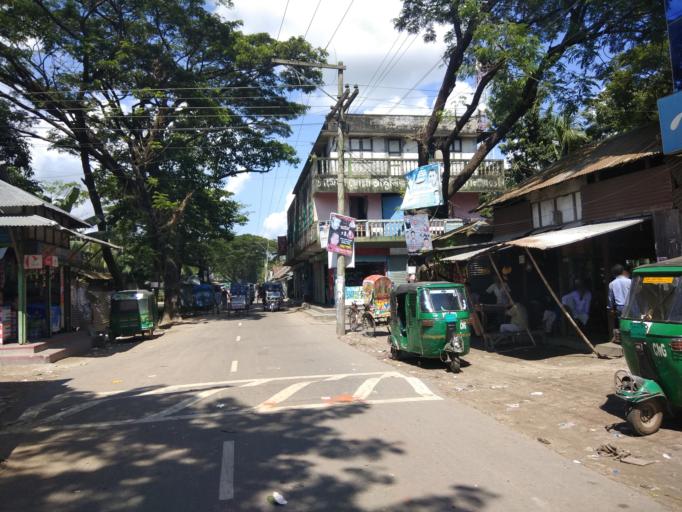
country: BD
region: Dhaka
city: Narayanganj
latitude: 23.4331
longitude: 90.4887
